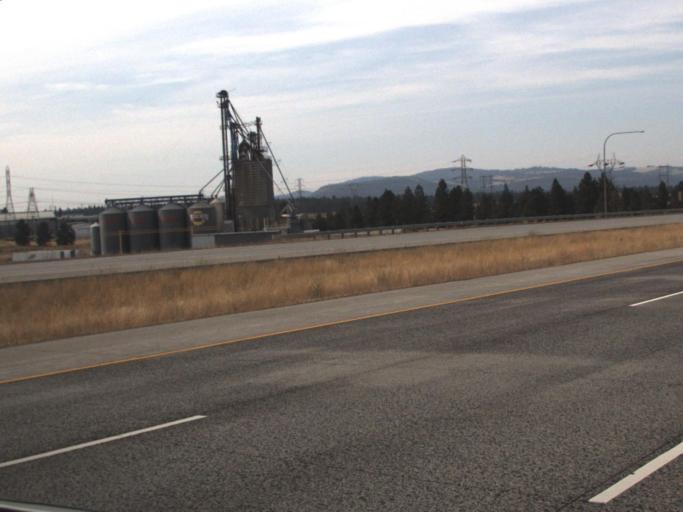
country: US
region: Washington
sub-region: Spokane County
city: Mead
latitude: 47.7549
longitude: -117.3612
